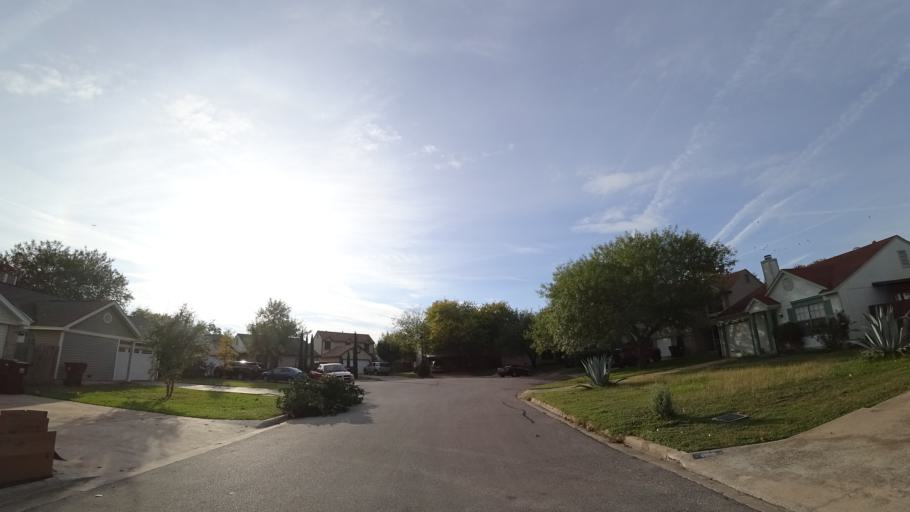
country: US
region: Texas
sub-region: Williamson County
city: Round Rock
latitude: 30.5017
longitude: -97.6667
